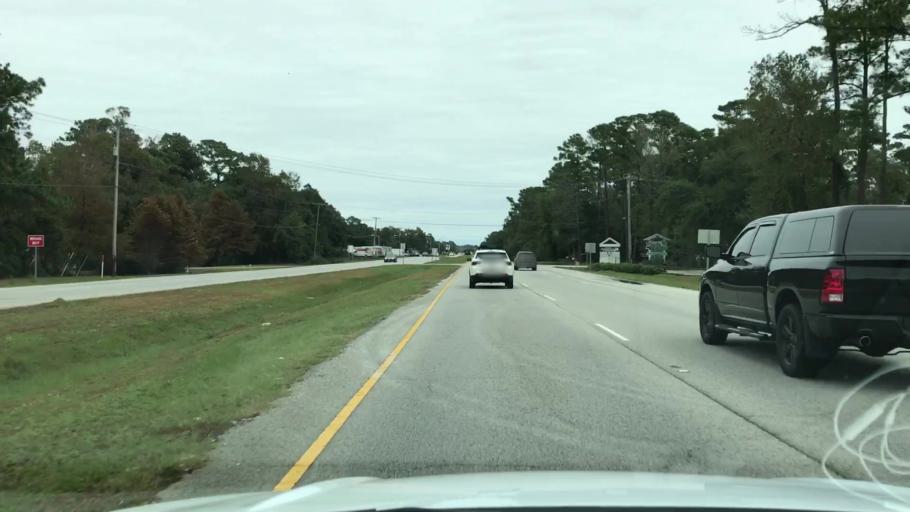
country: US
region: South Carolina
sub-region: Georgetown County
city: Murrells Inlet
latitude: 33.5424
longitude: -79.0532
